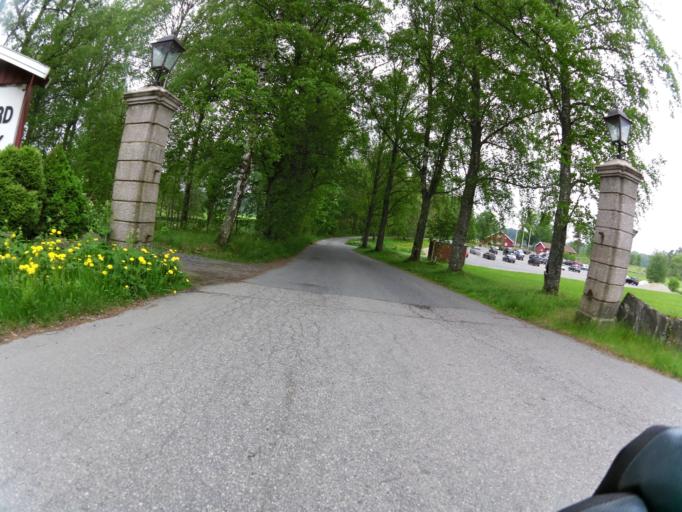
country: NO
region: Ostfold
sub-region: Rygge
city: Larkollen
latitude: 59.3681
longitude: 10.6838
